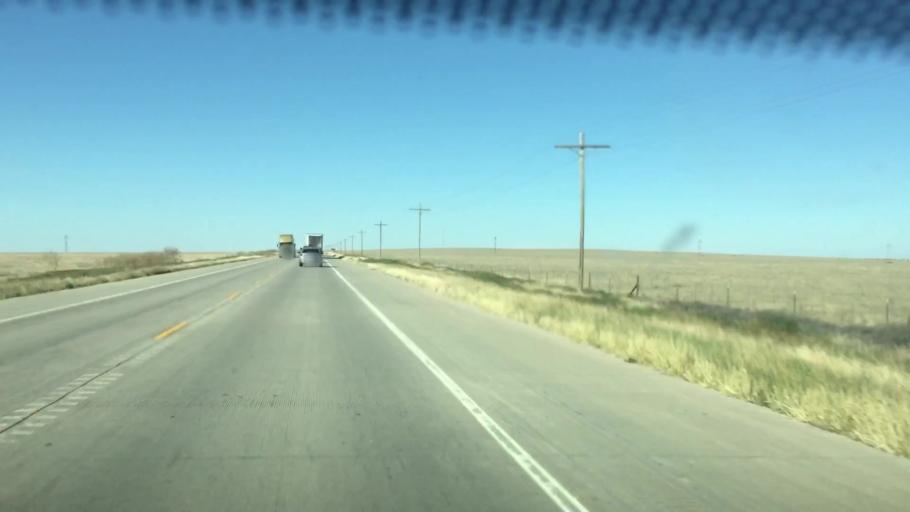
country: US
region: Colorado
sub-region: Prowers County
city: Lamar
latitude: 38.2544
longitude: -102.7239
